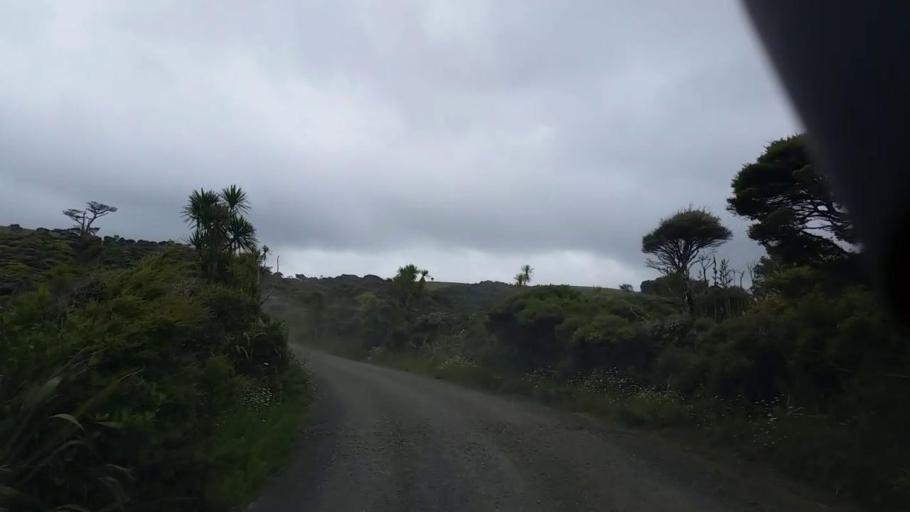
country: NZ
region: Auckland
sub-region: Auckland
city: Muriwai Beach
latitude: -36.9310
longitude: 174.4665
